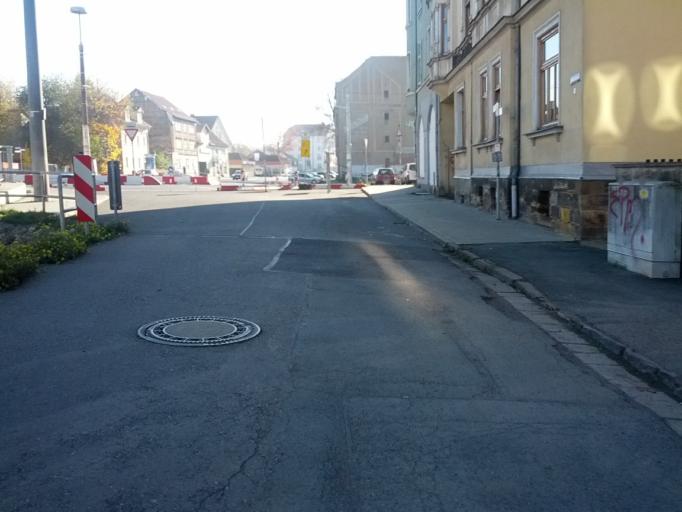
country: DE
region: Thuringia
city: Gotha
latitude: 50.9541
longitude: 10.7091
